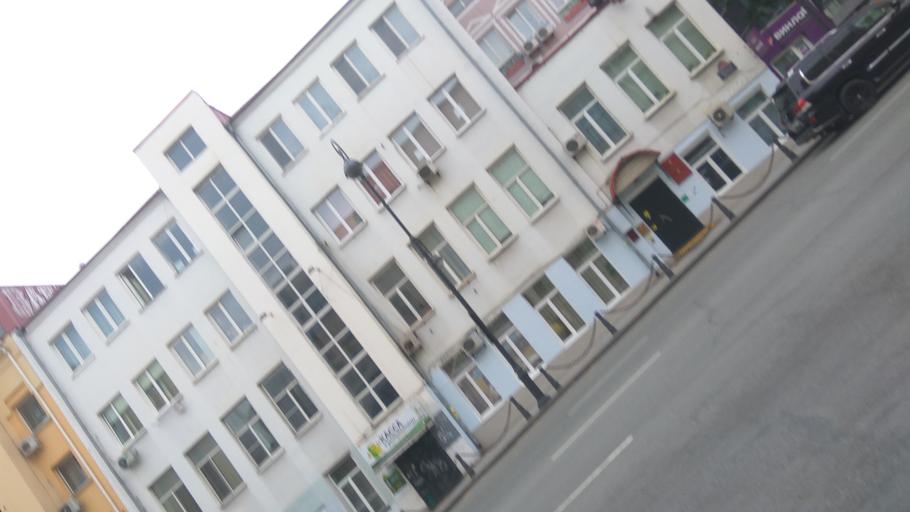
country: RU
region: Primorskiy
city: Vladivostok
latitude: 43.1191
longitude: 131.8869
